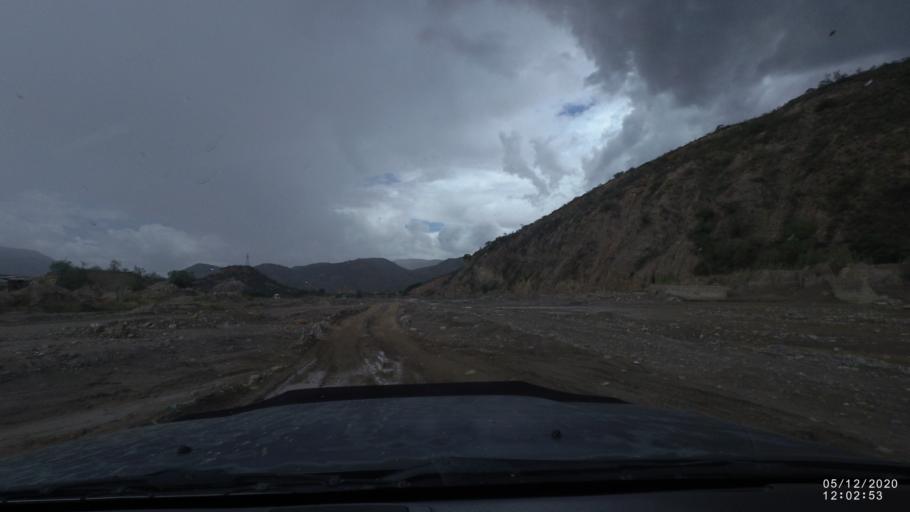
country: BO
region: Cochabamba
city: Sipe Sipe
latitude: -17.5732
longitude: -66.3510
